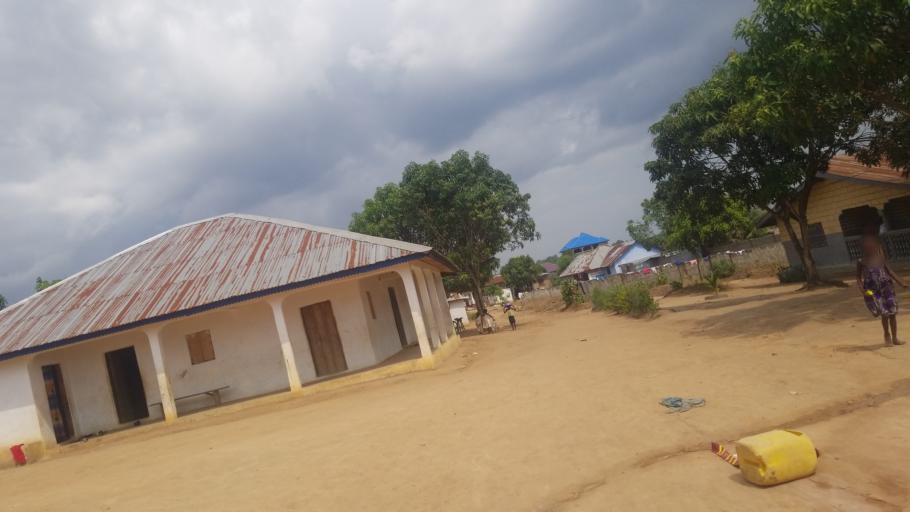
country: SL
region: Western Area
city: Waterloo
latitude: 8.3238
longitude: -13.0409
